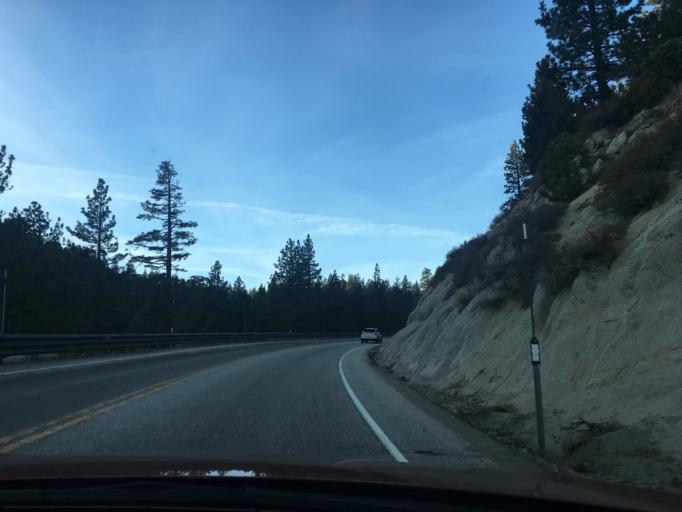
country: US
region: Nevada
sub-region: Douglas County
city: Kingsbury
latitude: 38.9746
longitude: -119.8794
